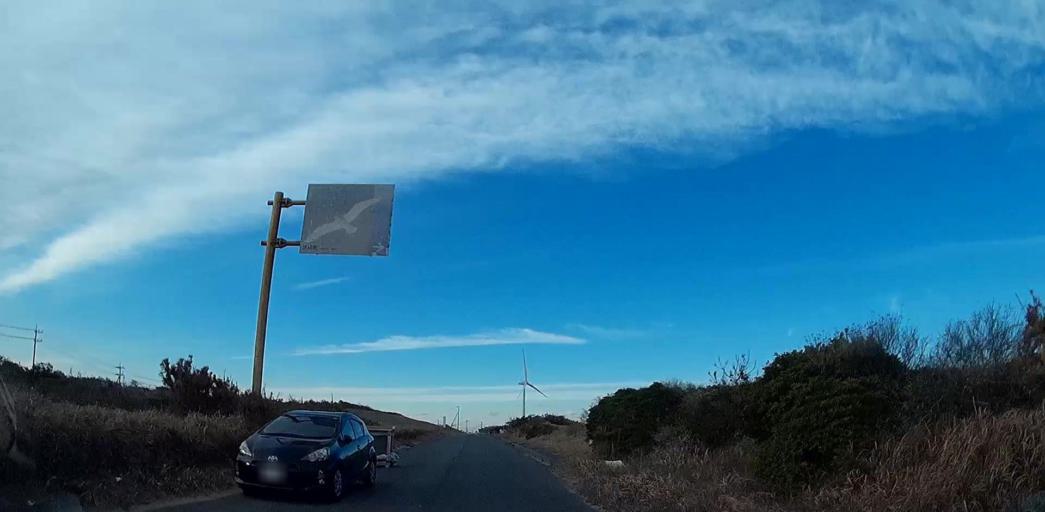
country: JP
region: Chiba
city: Hasaki
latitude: 35.7871
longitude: 140.8014
